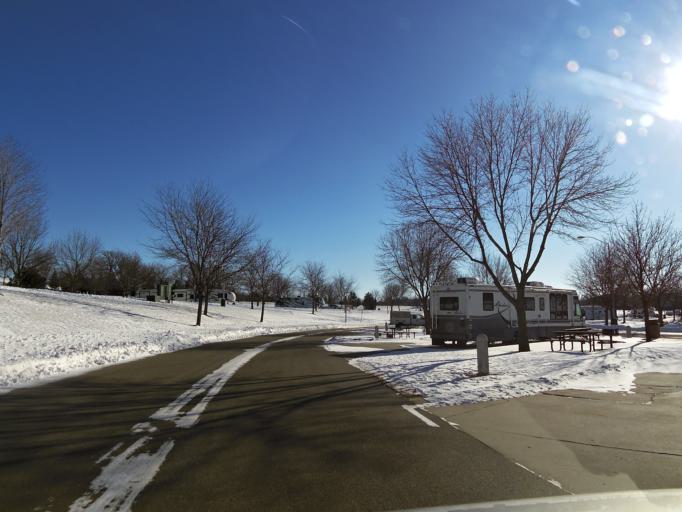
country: US
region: Minnesota
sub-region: Scott County
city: Prior Lake
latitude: 44.7281
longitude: -93.4719
